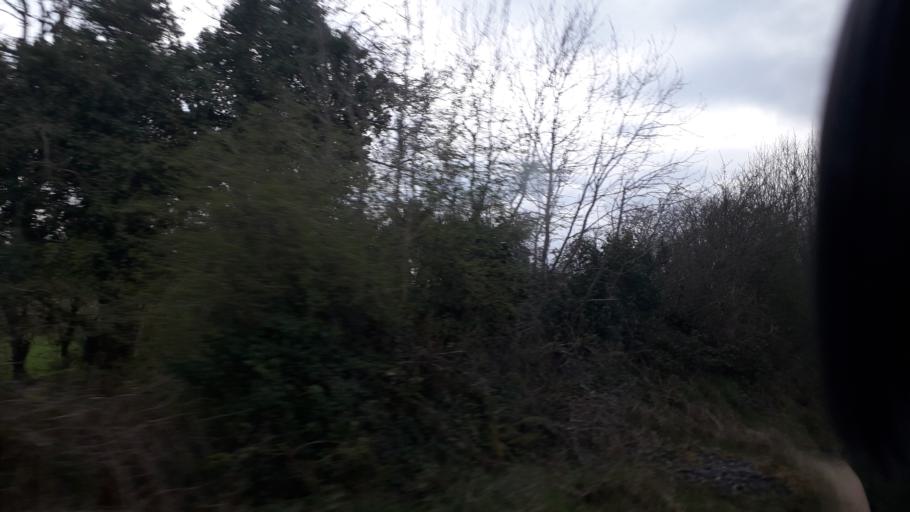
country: IE
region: Leinster
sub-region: An Longfort
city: Longford
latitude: 53.7068
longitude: -7.7176
